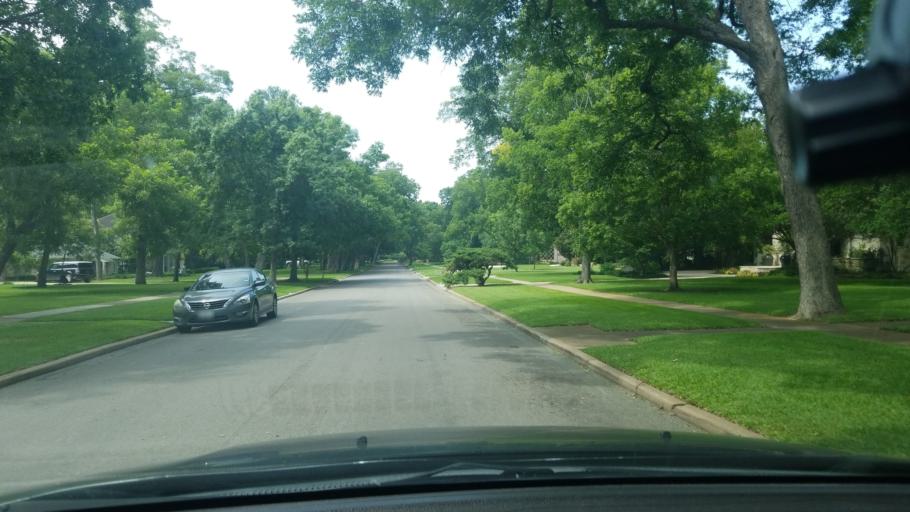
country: US
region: Texas
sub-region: Dallas County
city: Highland Park
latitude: 32.8155
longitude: -96.7138
